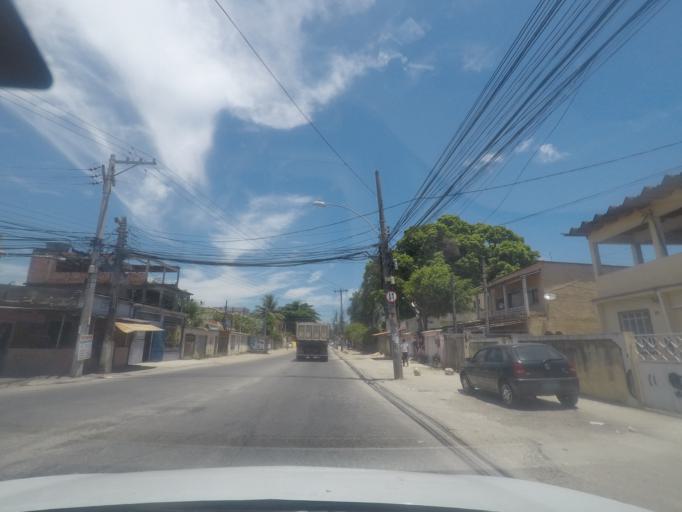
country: BR
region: Rio de Janeiro
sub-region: Itaguai
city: Itaguai
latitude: -22.9356
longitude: -43.6884
